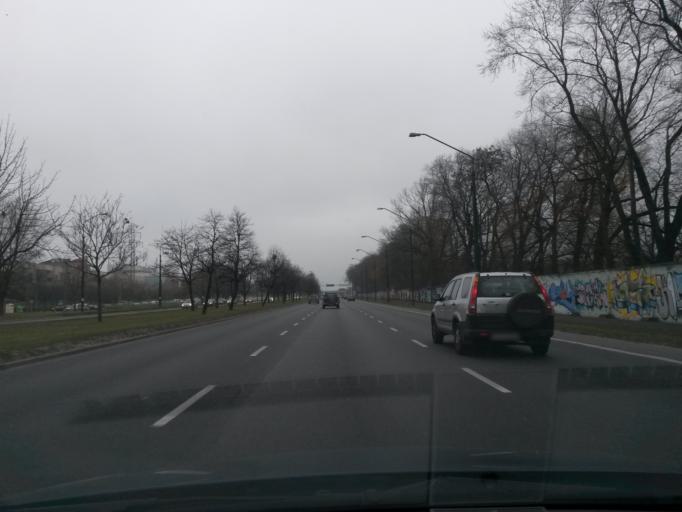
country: PL
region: Masovian Voivodeship
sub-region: Warszawa
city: Ursynow
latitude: 52.1596
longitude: 21.0173
